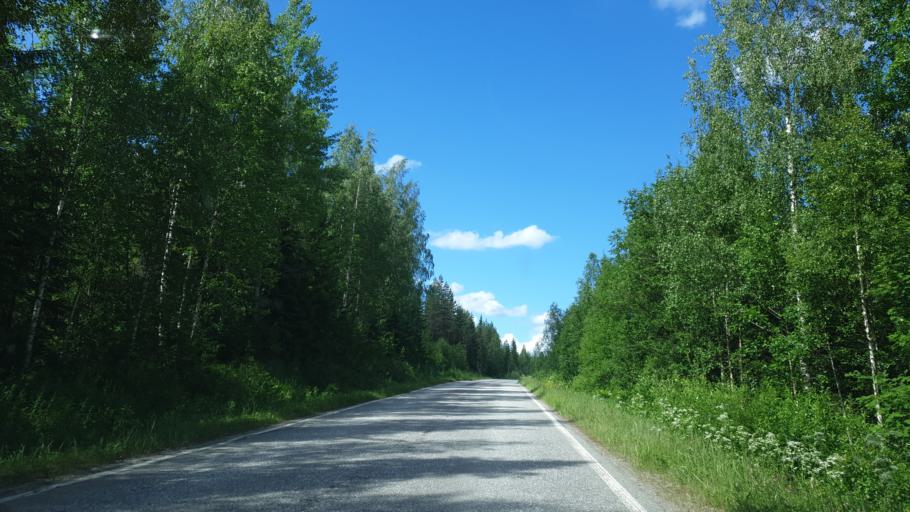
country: FI
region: Northern Savo
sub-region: Koillis-Savo
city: Kaavi
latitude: 63.0332
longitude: 28.6077
